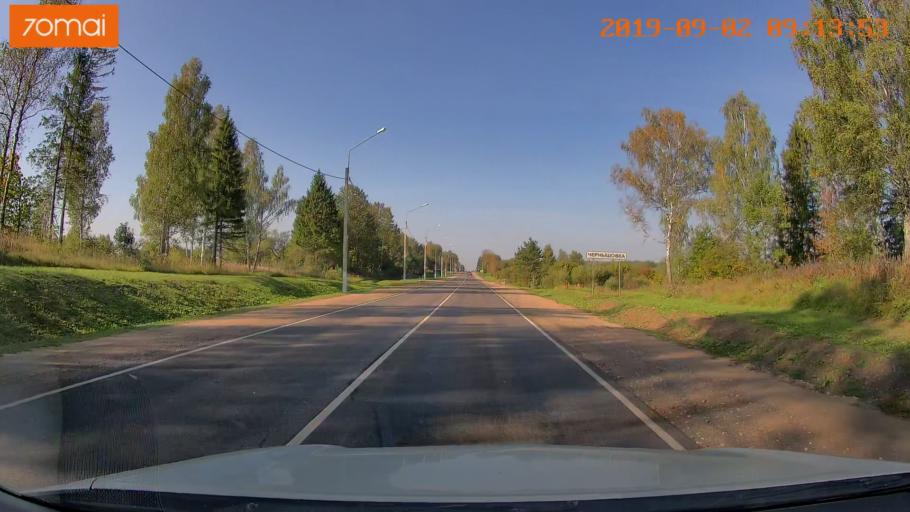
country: RU
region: Kaluga
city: Nikola-Lenivets
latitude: 54.8500
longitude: 35.5253
